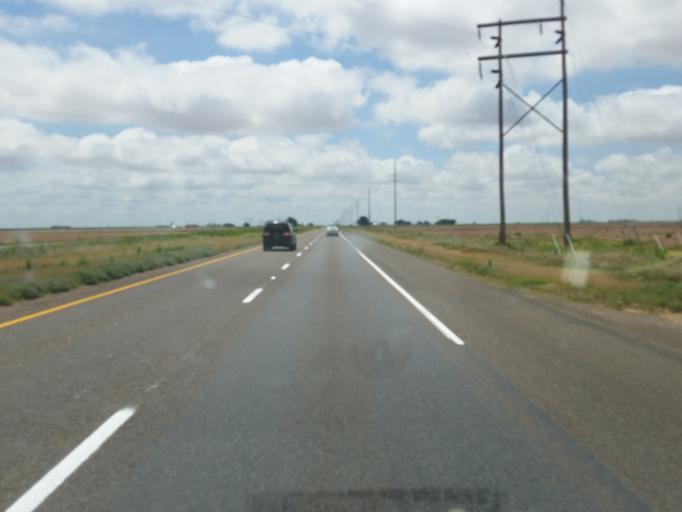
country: US
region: Texas
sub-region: Lubbock County
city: Slaton
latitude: 33.4086
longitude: -101.6248
